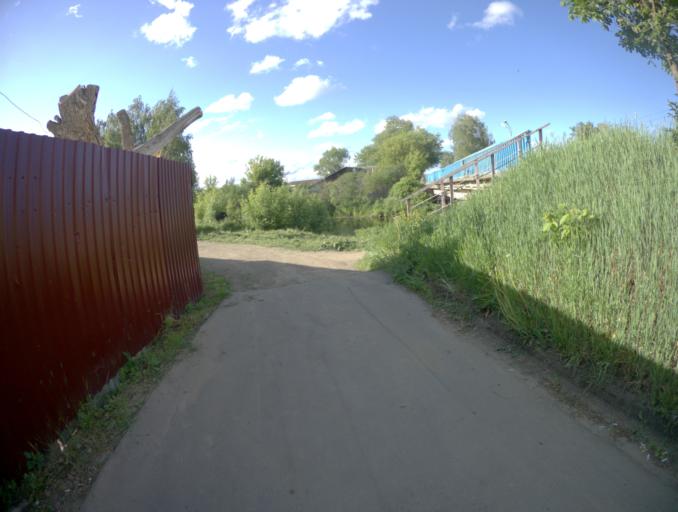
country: RU
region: Vladimir
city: Yur'yev-Pol'skiy
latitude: 56.4956
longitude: 39.6769
